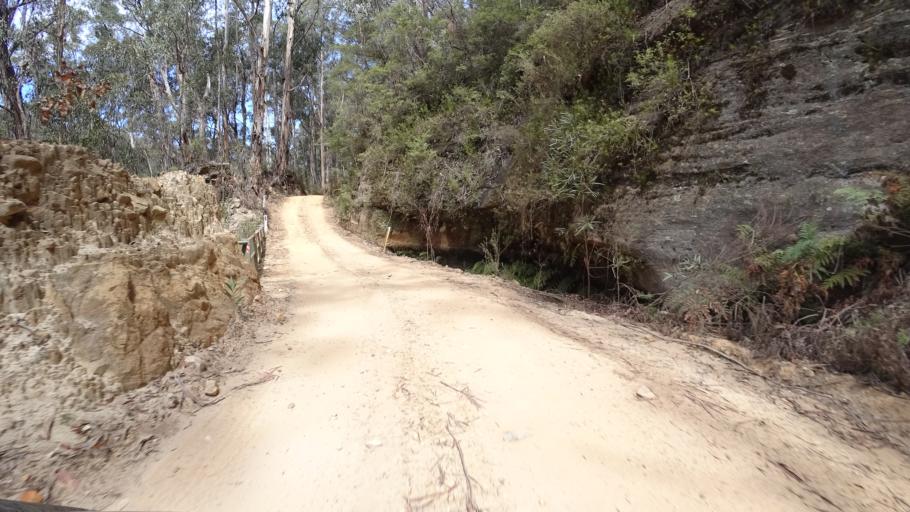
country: AU
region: New South Wales
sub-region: Lithgow
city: Lithgow
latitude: -33.2490
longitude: 150.2221
